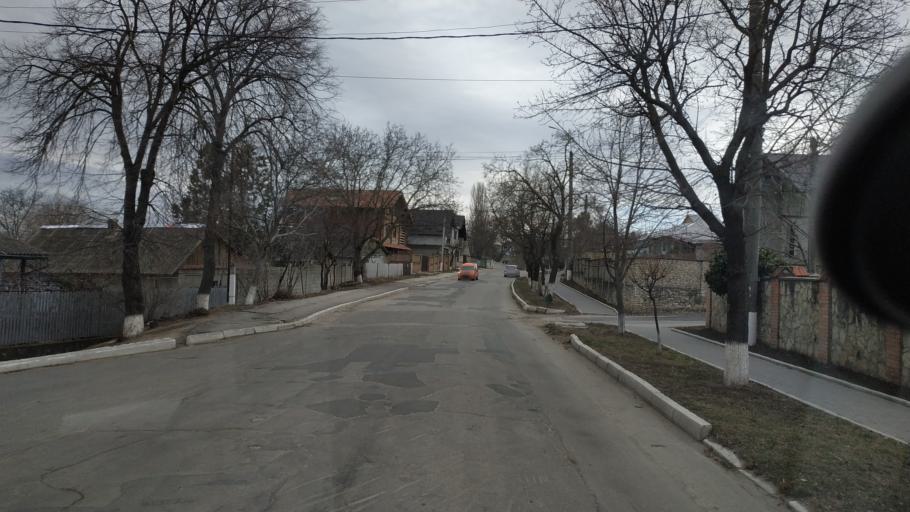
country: MD
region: Chisinau
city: Vadul lui Voda
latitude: 47.0915
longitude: 29.0761
